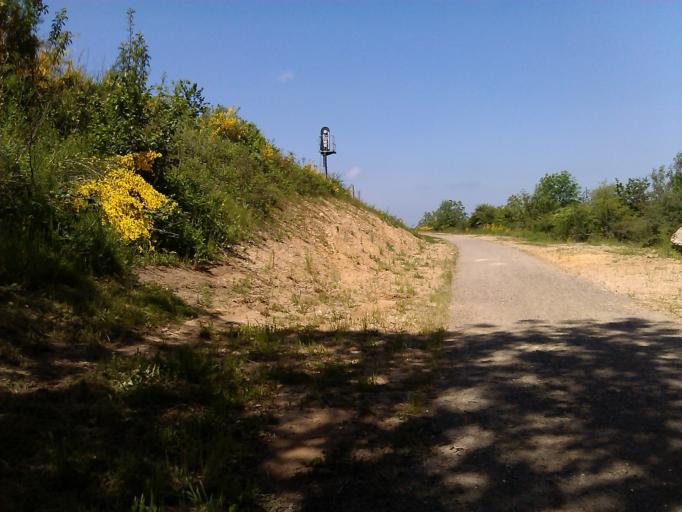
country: FR
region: Centre
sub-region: Departement de l'Indre
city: Saint-Marcel
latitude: 46.6096
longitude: 1.4968
